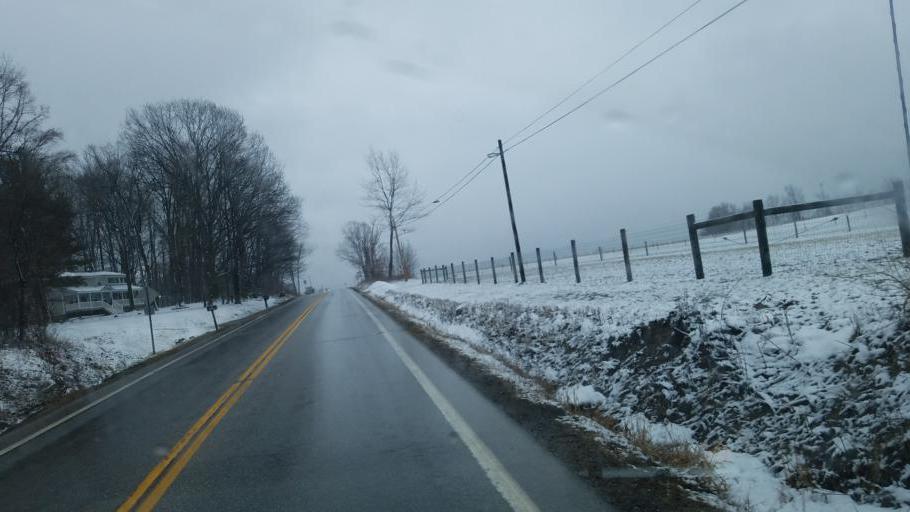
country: US
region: Ohio
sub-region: Geauga County
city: Middlefield
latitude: 41.3798
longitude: -81.0735
